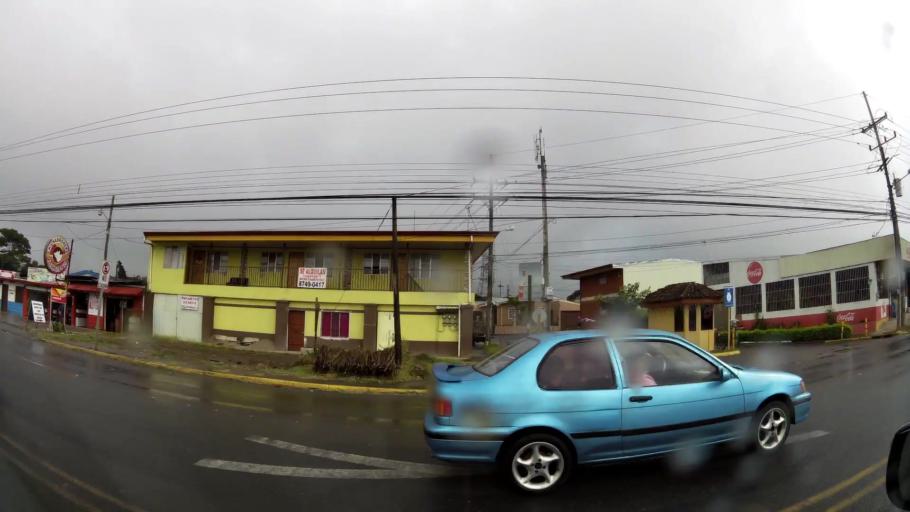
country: CR
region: Cartago
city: Paraiso
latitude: 9.8473
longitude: -83.8940
